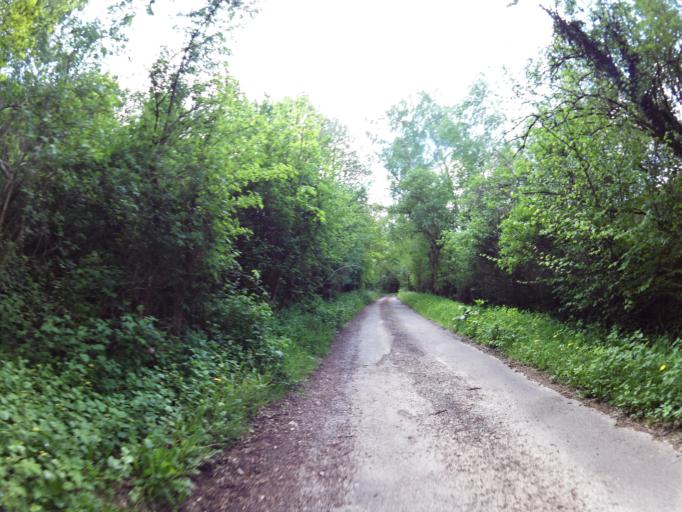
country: DE
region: North Rhine-Westphalia
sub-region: Regierungsbezirk Koln
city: Herzogenrath
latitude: 50.8974
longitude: 6.0830
